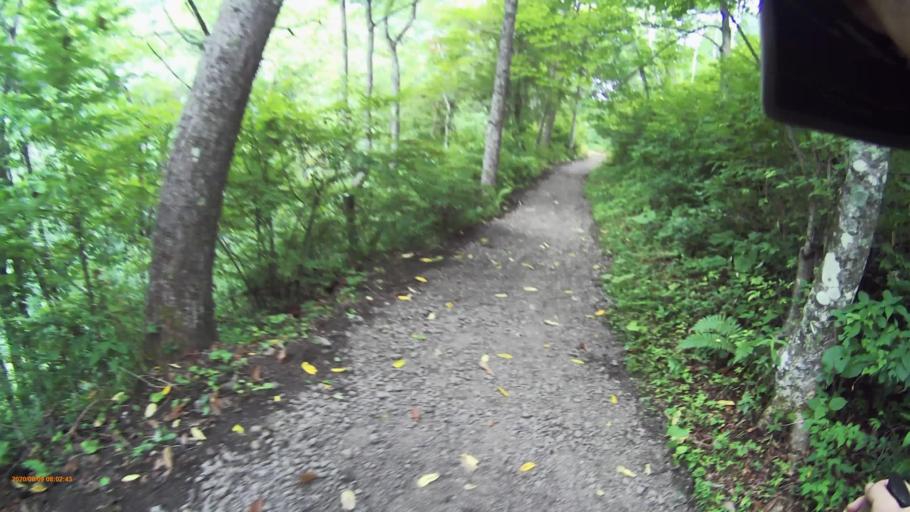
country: JP
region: Nagano
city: Ina
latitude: 35.9535
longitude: 137.7978
